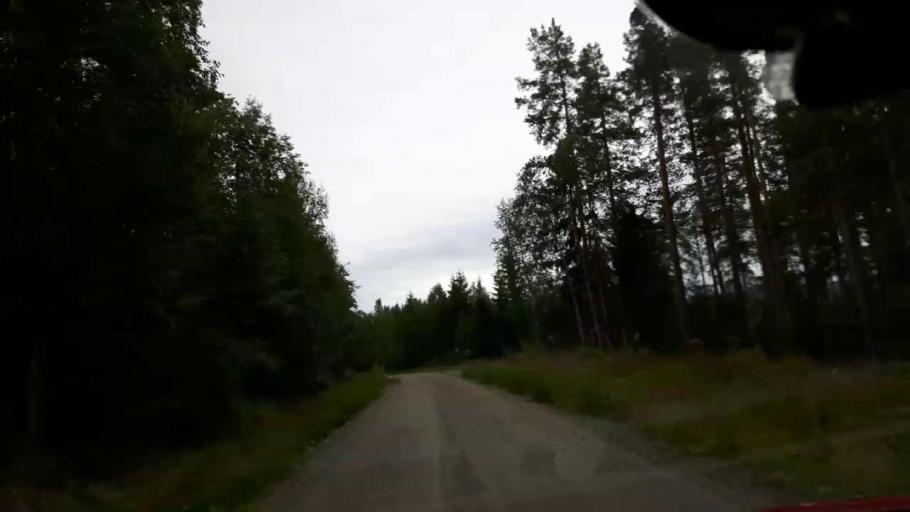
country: SE
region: Vaesternorrland
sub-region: Ange Kommun
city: Ange
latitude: 62.7851
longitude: 15.7733
